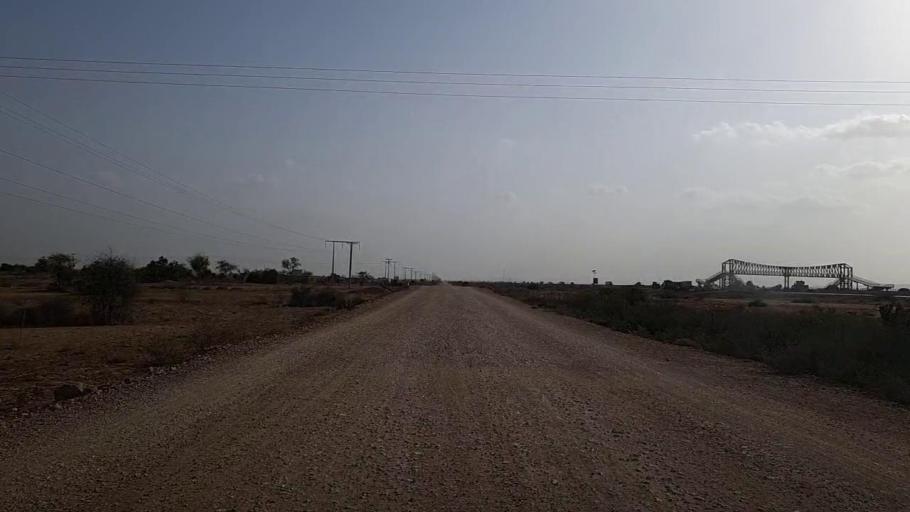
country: PK
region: Sindh
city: Kotri
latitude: 25.2315
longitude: 67.9299
